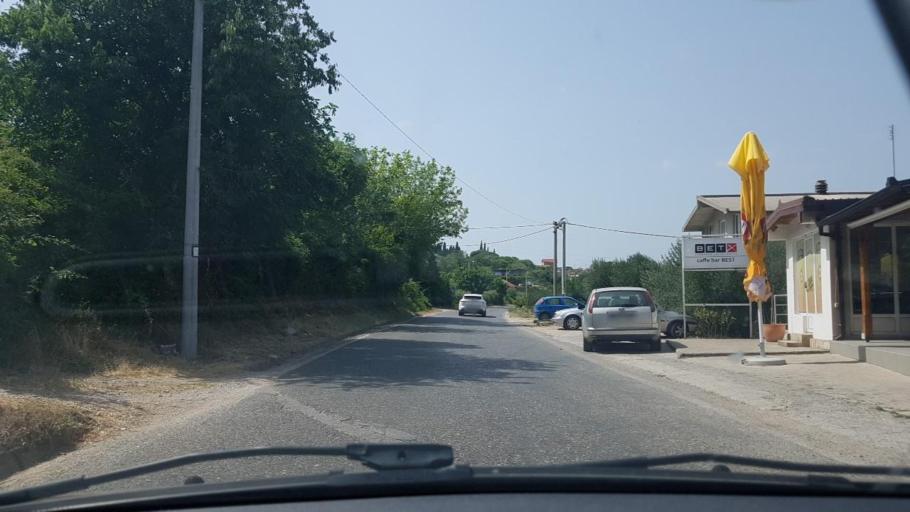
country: HR
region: Dubrovacko-Neretvanska
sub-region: Grad Dubrovnik
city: Metkovic
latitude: 43.0463
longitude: 17.7049
